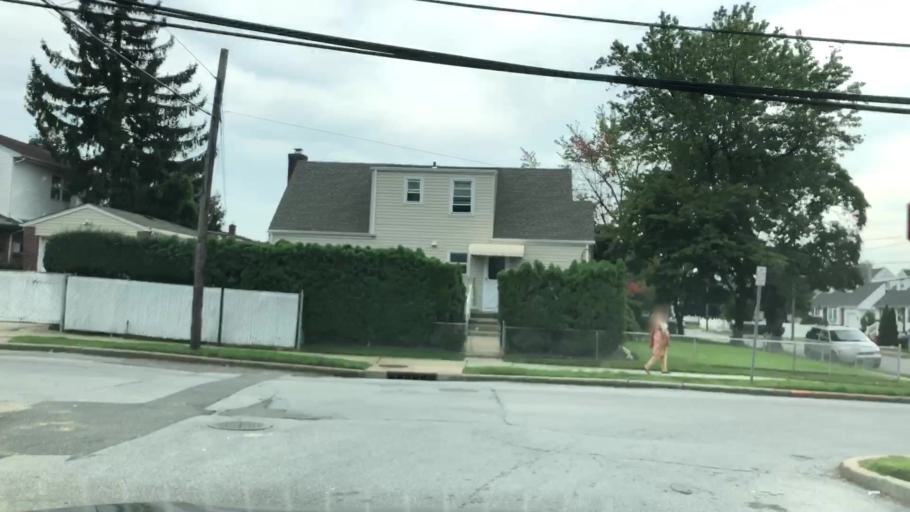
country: US
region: New York
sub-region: Nassau County
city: South Floral Park
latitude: 40.7012
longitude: -73.6915
